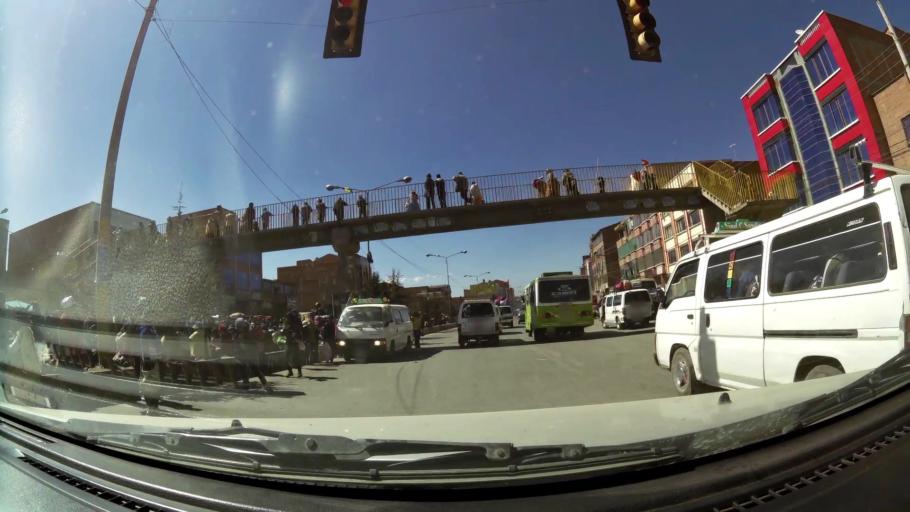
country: BO
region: La Paz
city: La Paz
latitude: -16.4913
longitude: -68.2016
